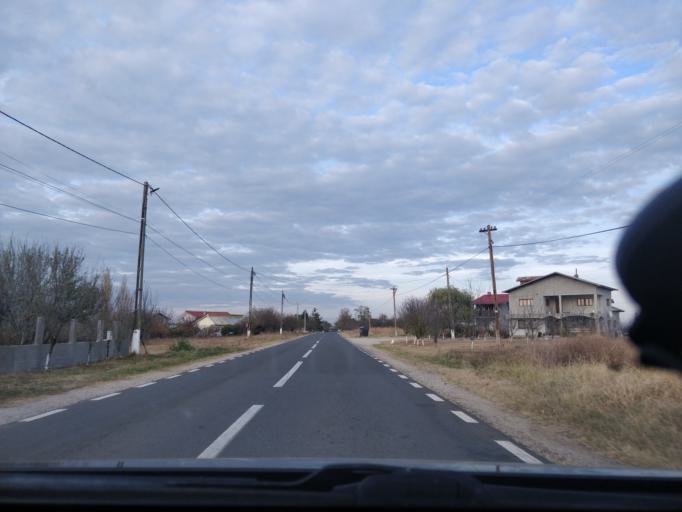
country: RO
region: Giurgiu
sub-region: Comuna Bucsani
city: Bucsani
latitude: 44.3823
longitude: 25.6574
